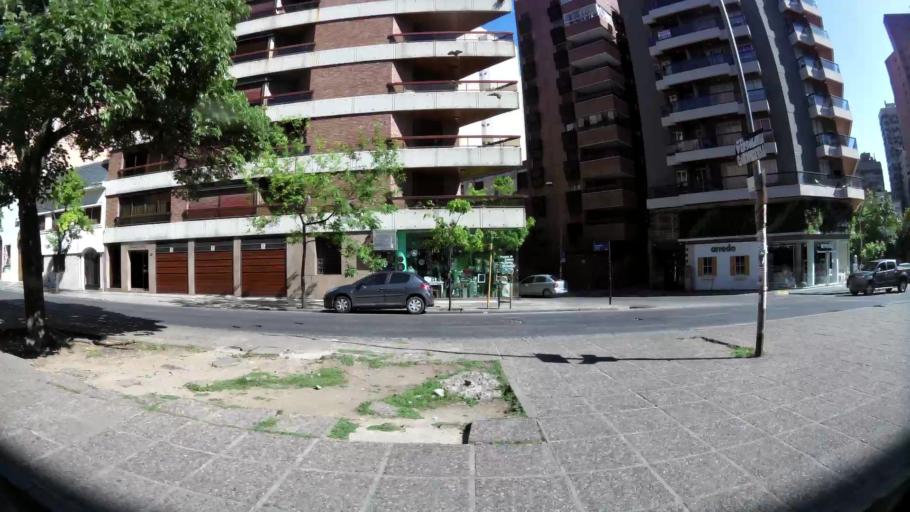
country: AR
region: Cordoba
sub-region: Departamento de Capital
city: Cordoba
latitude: -31.4295
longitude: -64.1868
